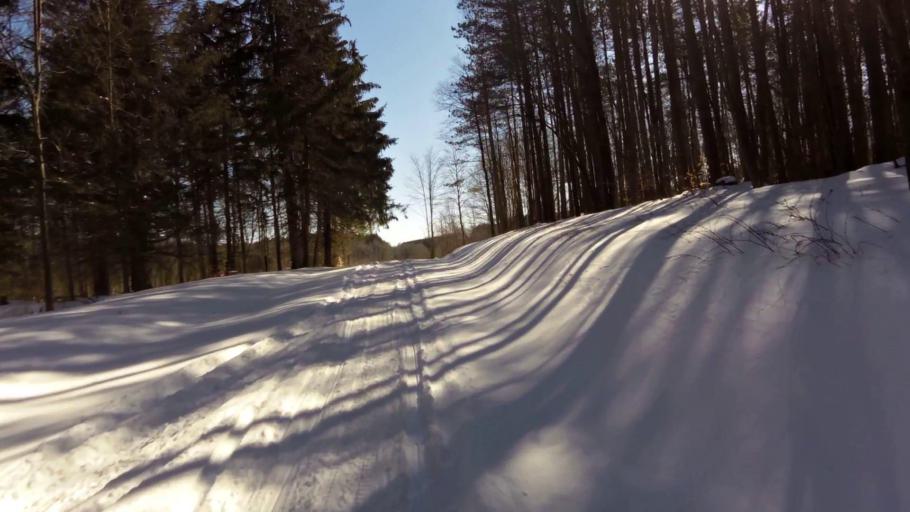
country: US
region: New York
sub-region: Allegany County
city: Cuba
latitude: 42.3051
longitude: -78.2584
